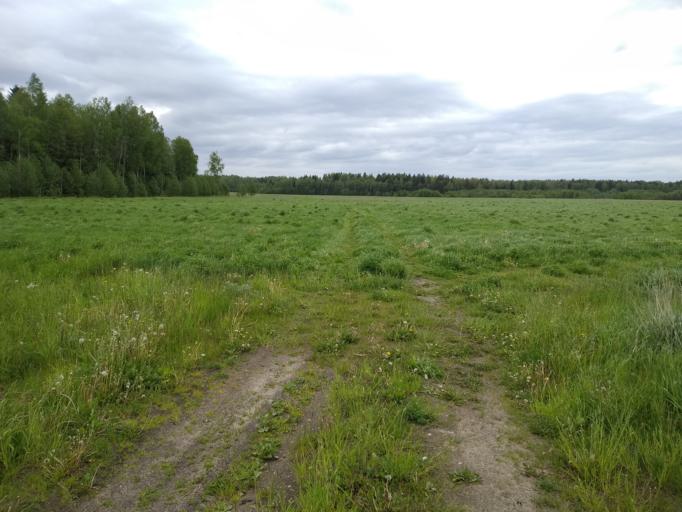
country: BY
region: Grodnenskaya
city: Mir
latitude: 53.5966
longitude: 26.5462
